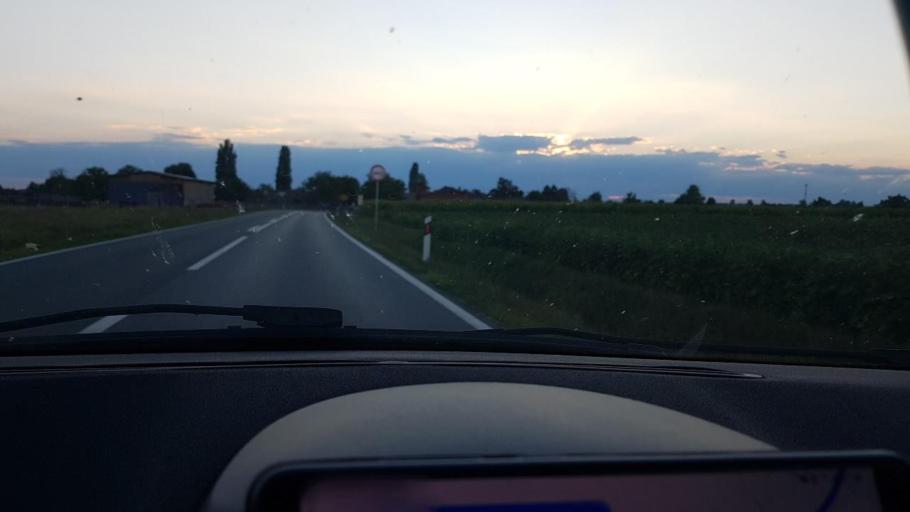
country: HR
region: Bjelovarsko-Bilogorska
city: Zdralovi
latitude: 45.8517
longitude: 16.9354
